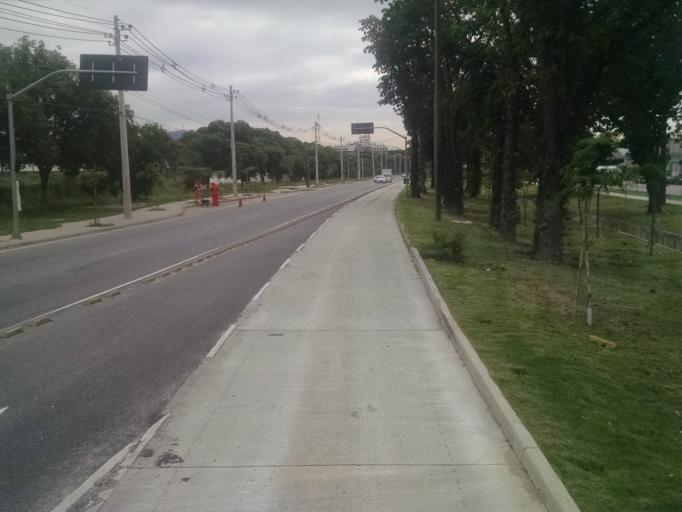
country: BR
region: Rio de Janeiro
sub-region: Sao Joao De Meriti
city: Sao Joao de Meriti
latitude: -22.9432
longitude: -43.3725
